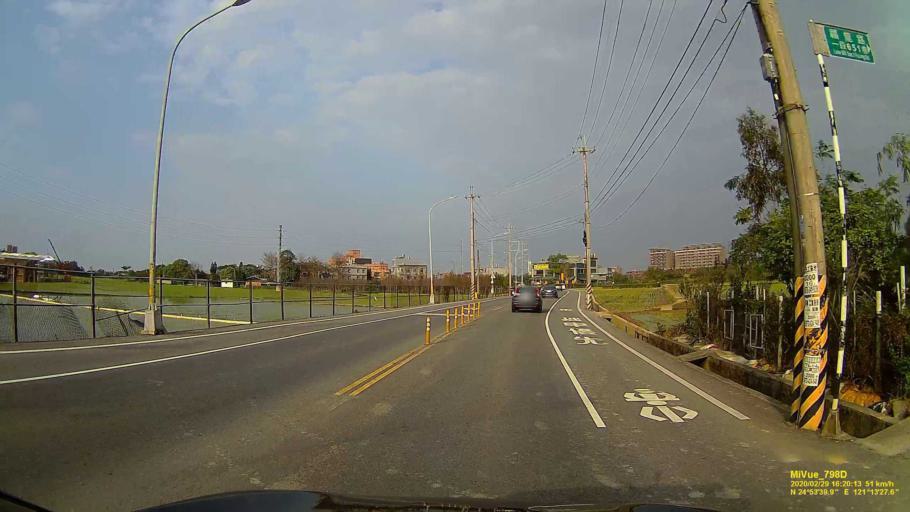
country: TW
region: Taiwan
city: Daxi
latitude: 24.8948
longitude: 121.2246
